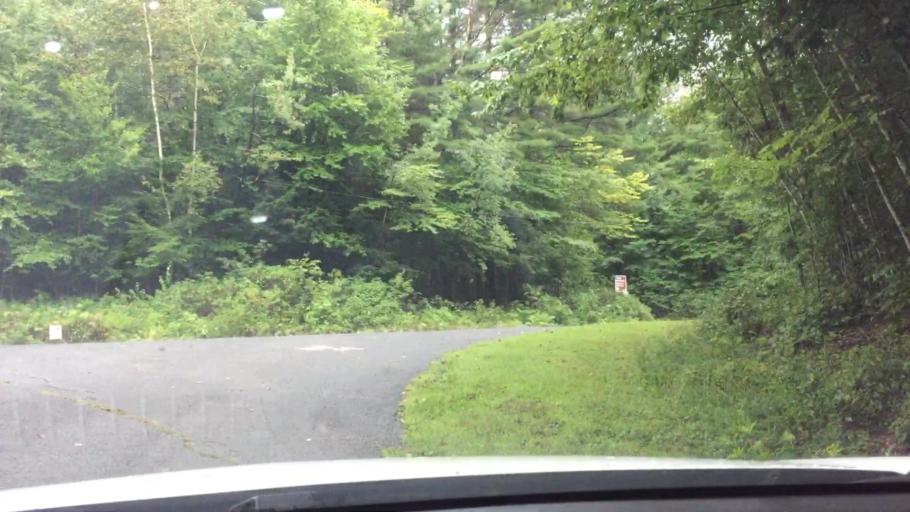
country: US
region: Massachusetts
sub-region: Berkshire County
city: Otis
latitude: 42.1450
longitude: -73.0494
